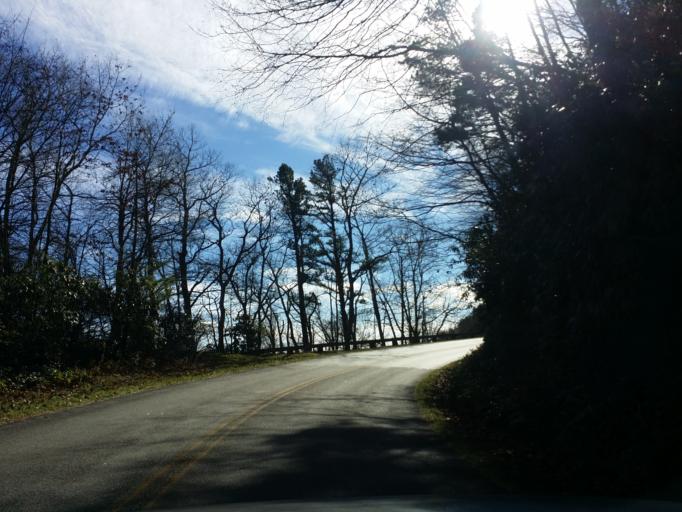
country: US
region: North Carolina
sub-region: Buncombe County
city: Black Mountain
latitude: 35.7305
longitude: -82.2041
